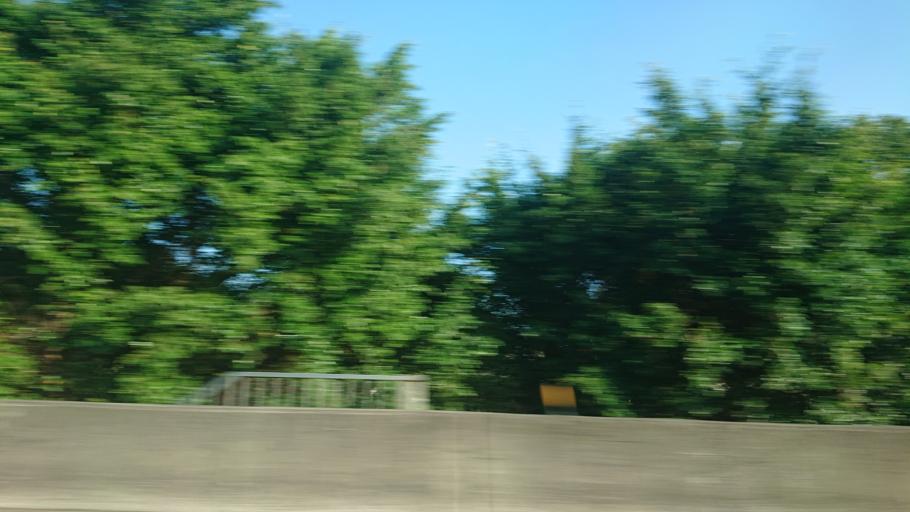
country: TW
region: Taiwan
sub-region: Changhua
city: Chang-hua
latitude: 24.1215
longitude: 120.6162
